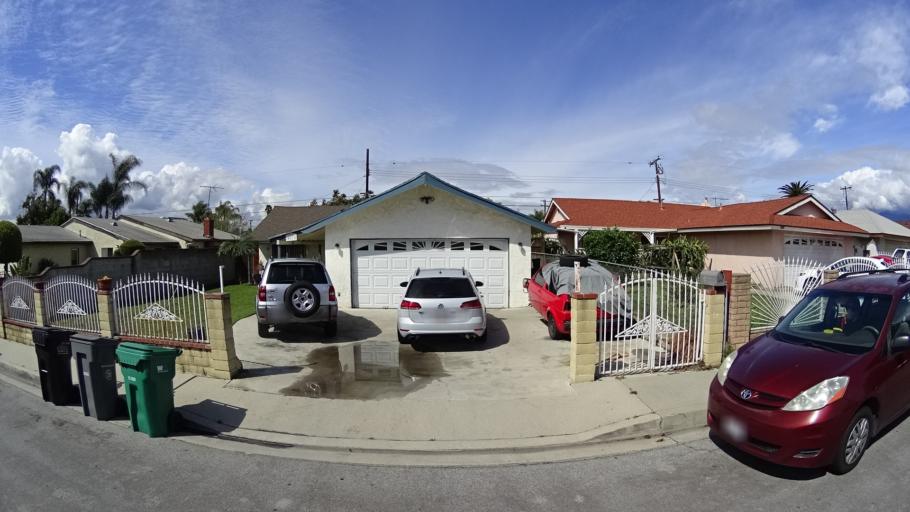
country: US
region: California
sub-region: Los Angeles County
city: Baldwin Park
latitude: 34.0859
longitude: -117.9800
